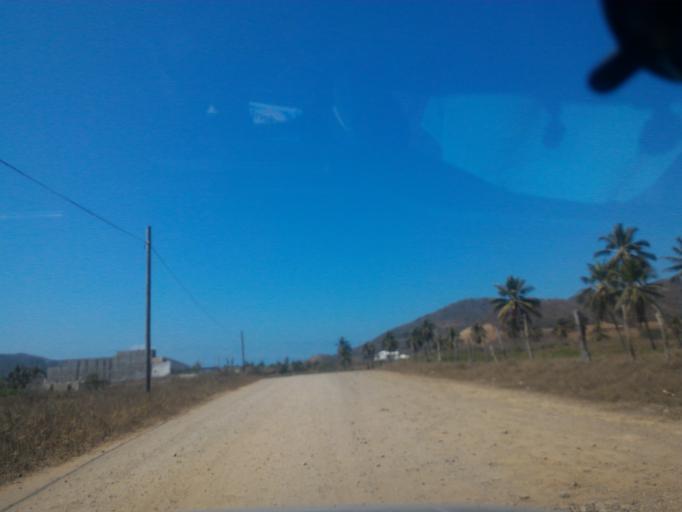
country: MX
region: Michoacan
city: Coahuayana Viejo
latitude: 18.5868
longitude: -103.6799
